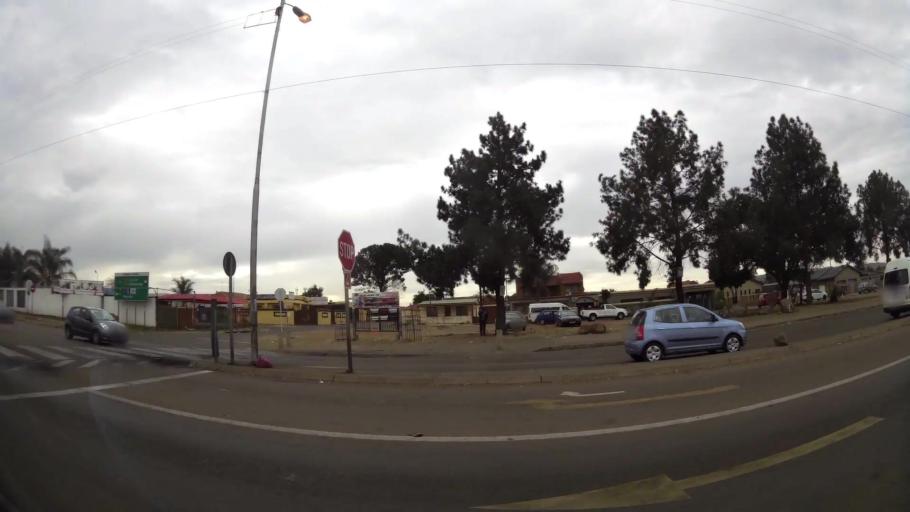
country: ZA
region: Gauteng
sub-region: City of Tshwane Metropolitan Municipality
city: Pretoria
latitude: -25.7184
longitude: 28.3487
